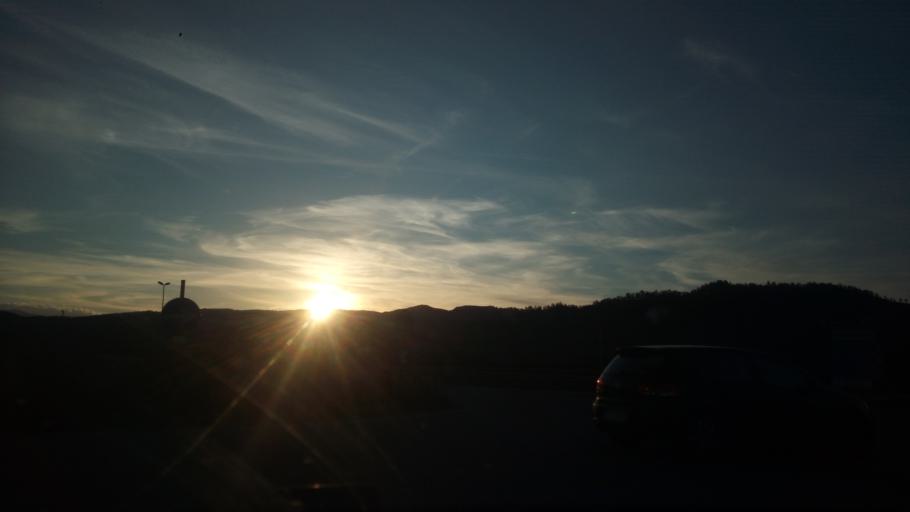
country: IT
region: Calabria
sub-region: Provincia di Catanzaro
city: Roccelletta
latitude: 38.8449
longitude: 16.5834
